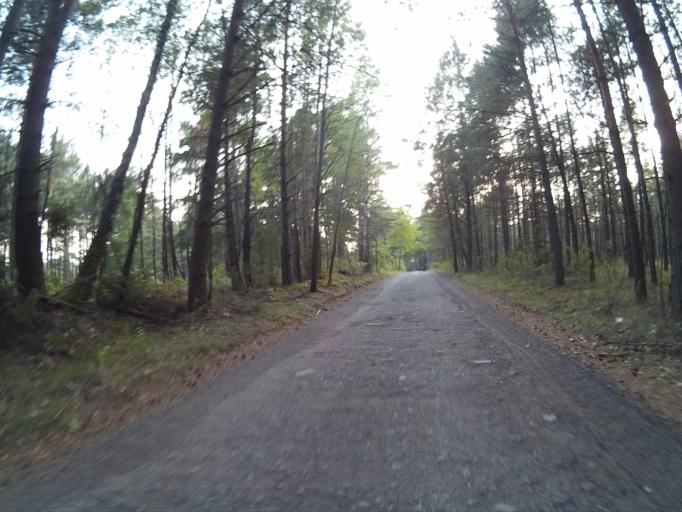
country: PL
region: Pomeranian Voivodeship
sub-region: Powiat chojnicki
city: Czersk
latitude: 53.7195
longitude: 17.9481
